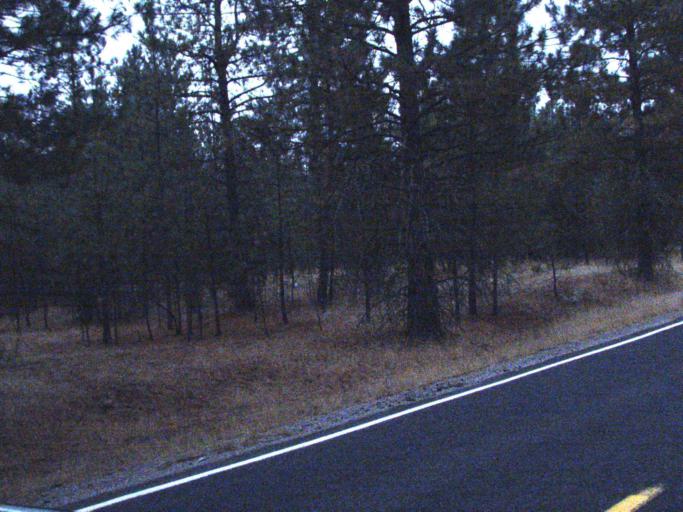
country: US
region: Washington
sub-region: Spokane County
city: Fairchild Air Force Base
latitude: 47.8955
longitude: -117.8241
